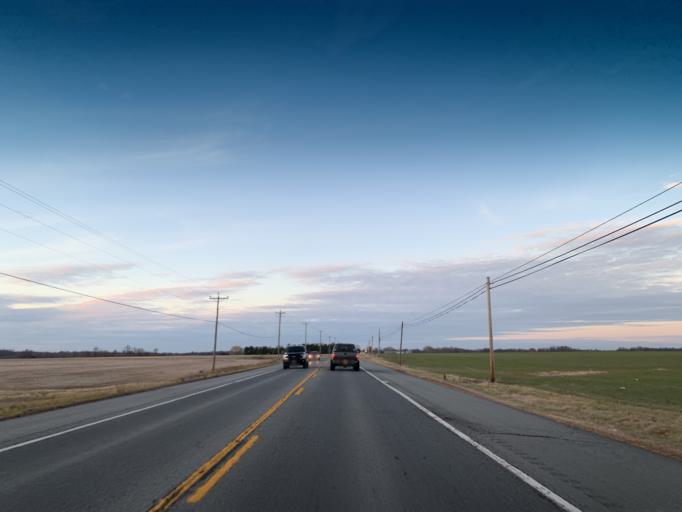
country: US
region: Delaware
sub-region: New Castle County
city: Middletown
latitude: 39.4280
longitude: -75.8604
